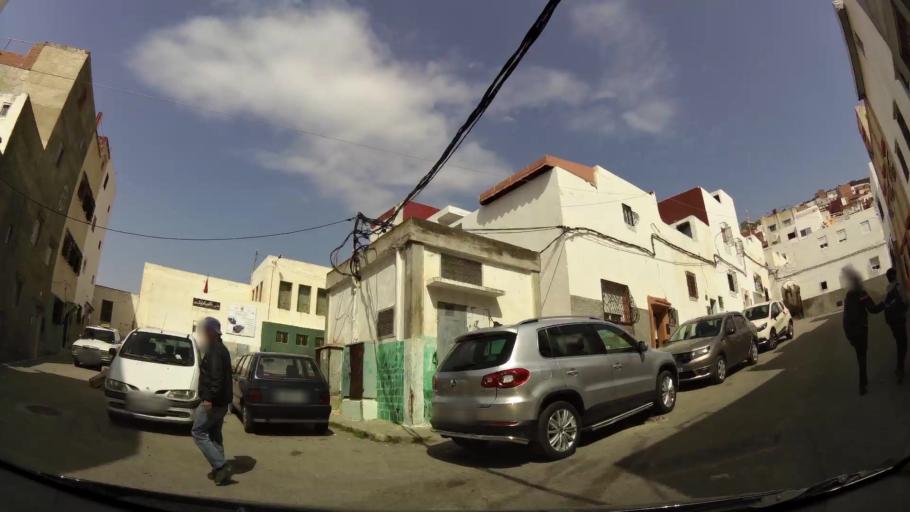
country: MA
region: Tanger-Tetouan
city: Tetouan
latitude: 35.5780
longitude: -5.3853
